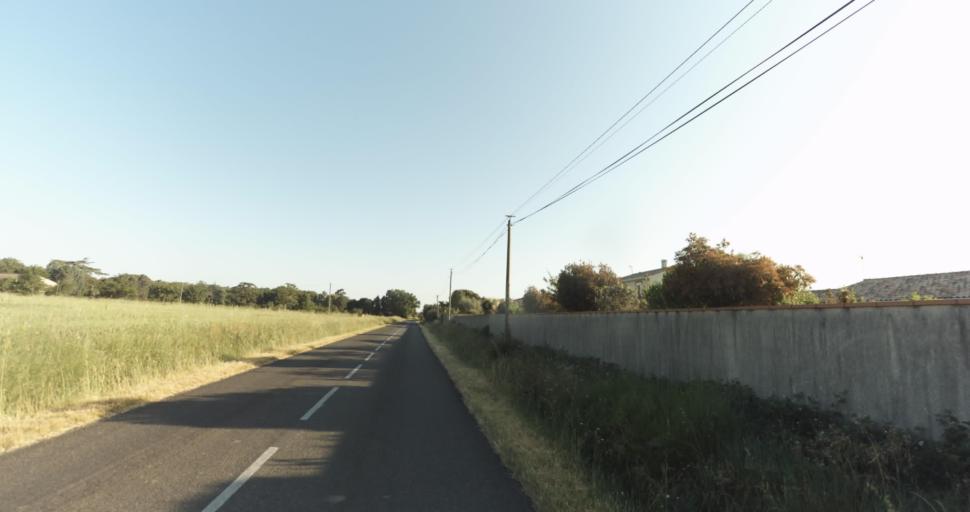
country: FR
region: Midi-Pyrenees
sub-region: Departement de la Haute-Garonne
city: Leguevin
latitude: 43.5889
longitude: 1.2365
